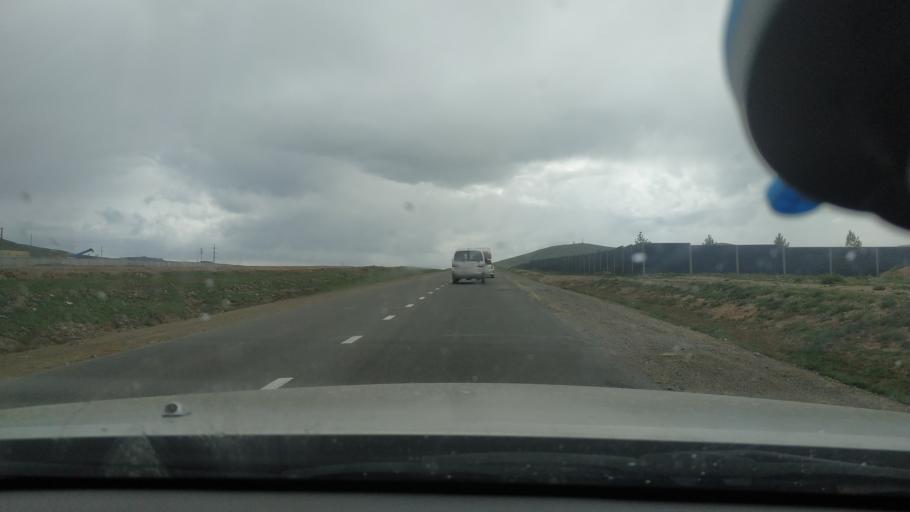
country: MN
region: Ulaanbaatar
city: Ulaanbaatar
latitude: 47.8052
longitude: 106.7492
